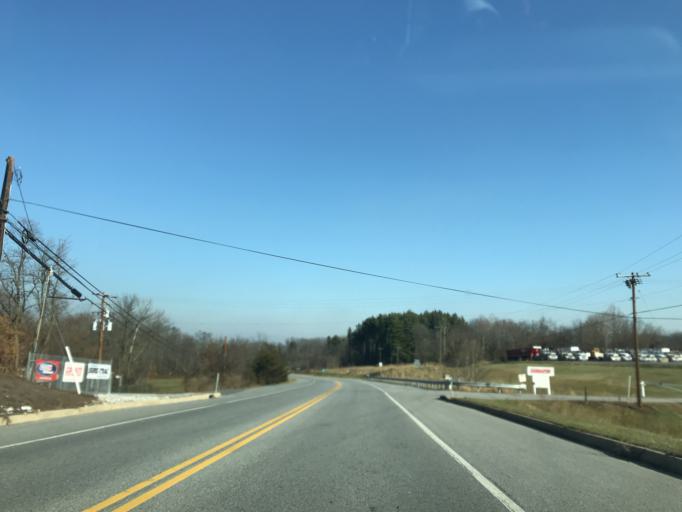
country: US
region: Maryland
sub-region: Carroll County
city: Taneytown
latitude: 39.6630
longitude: -77.1708
